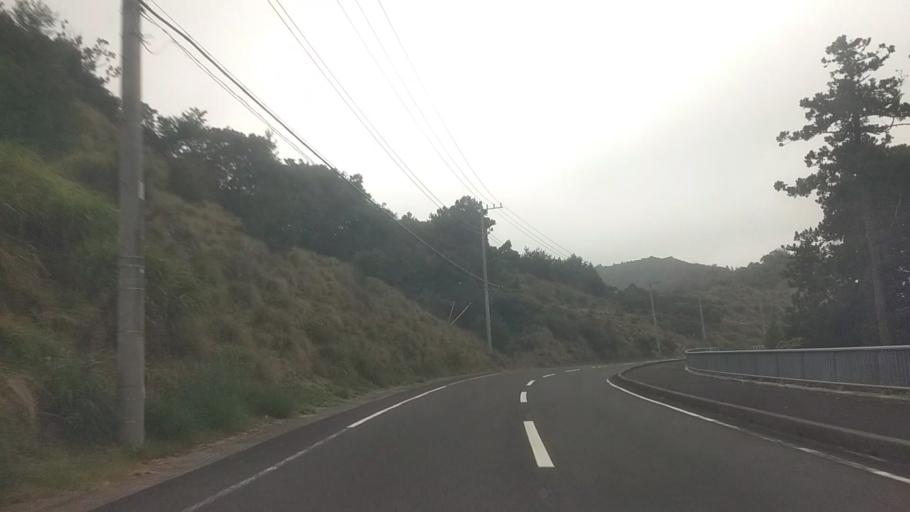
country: JP
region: Chiba
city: Kawaguchi
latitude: 35.1460
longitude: 140.1503
